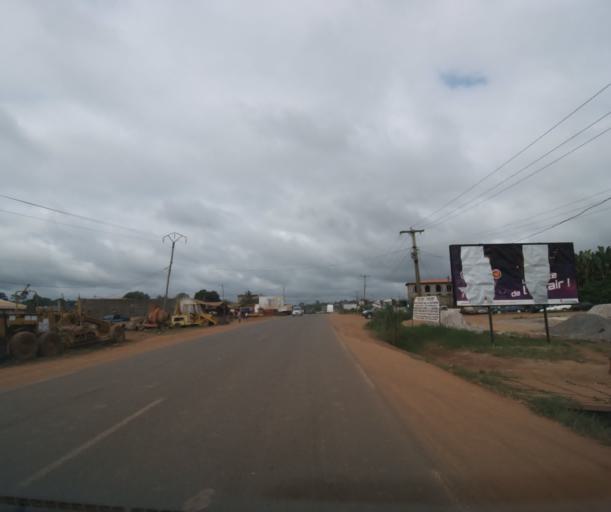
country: CM
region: Centre
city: Yaounde
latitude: 3.8013
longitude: 11.5062
